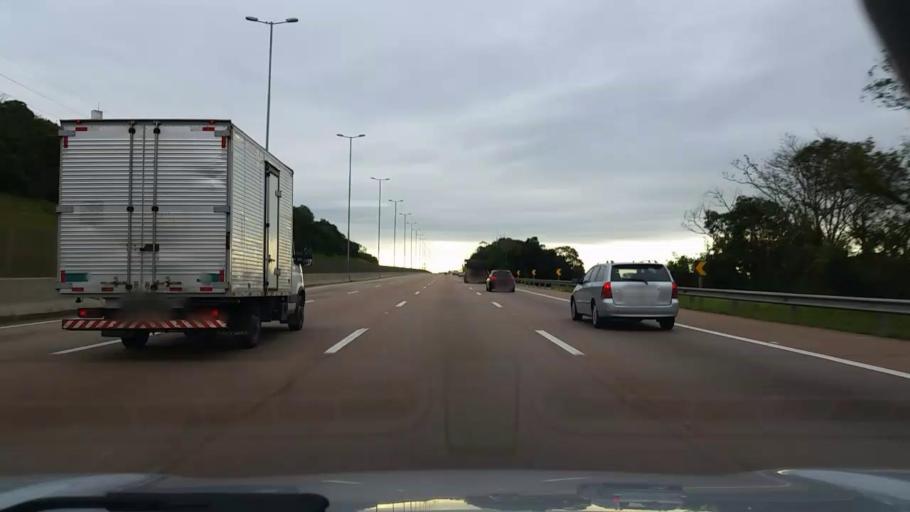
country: BR
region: Rio Grande do Sul
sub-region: Gravatai
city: Gravatai
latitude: -29.9564
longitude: -51.0117
